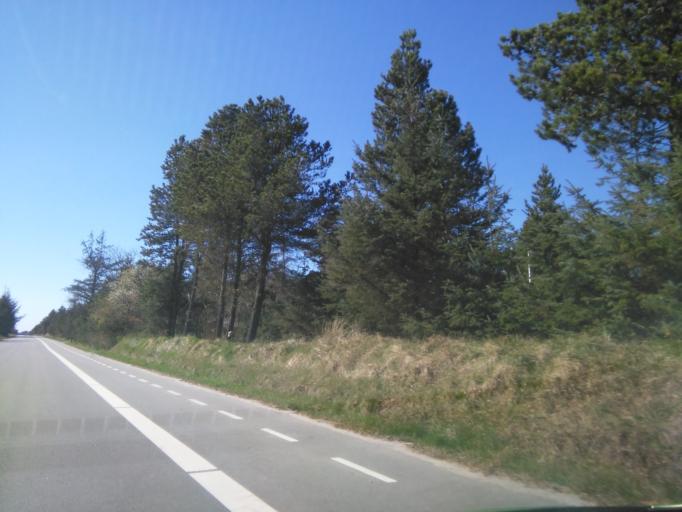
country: DK
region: South Denmark
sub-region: Varde Kommune
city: Oksbol
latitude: 55.5504
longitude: 8.2080
